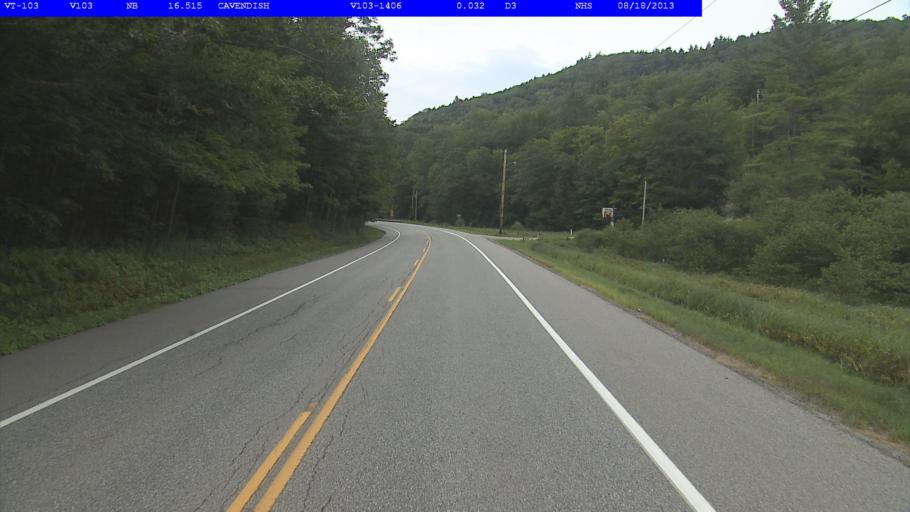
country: US
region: Vermont
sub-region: Windsor County
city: Chester
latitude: 43.3497
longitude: -72.6259
